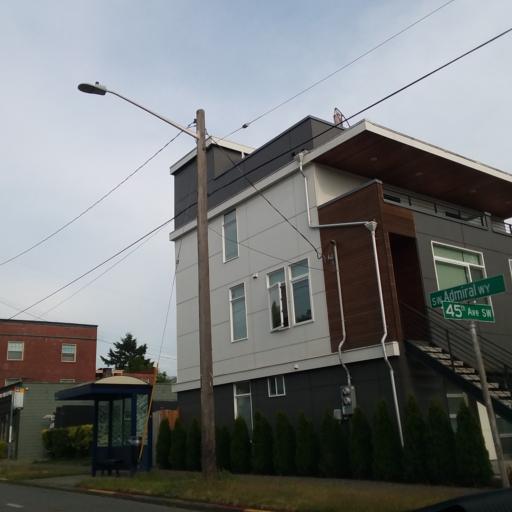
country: US
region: Washington
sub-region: King County
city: Seattle
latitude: 47.5812
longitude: -122.3892
